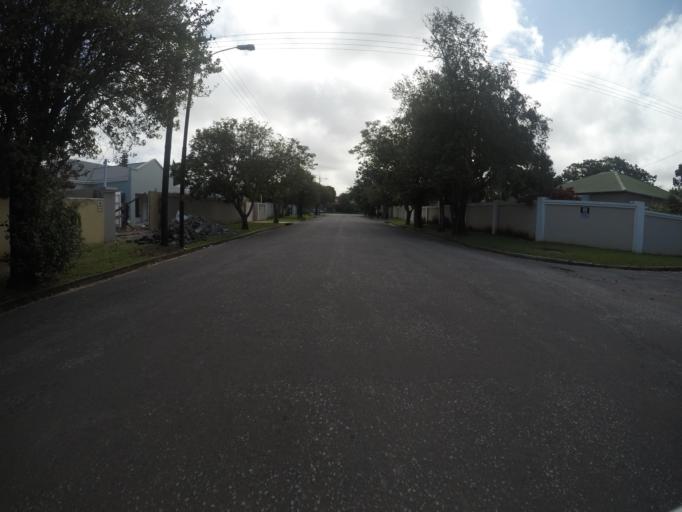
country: ZA
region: Eastern Cape
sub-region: Buffalo City Metropolitan Municipality
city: East London
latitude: -32.9762
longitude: 27.9035
